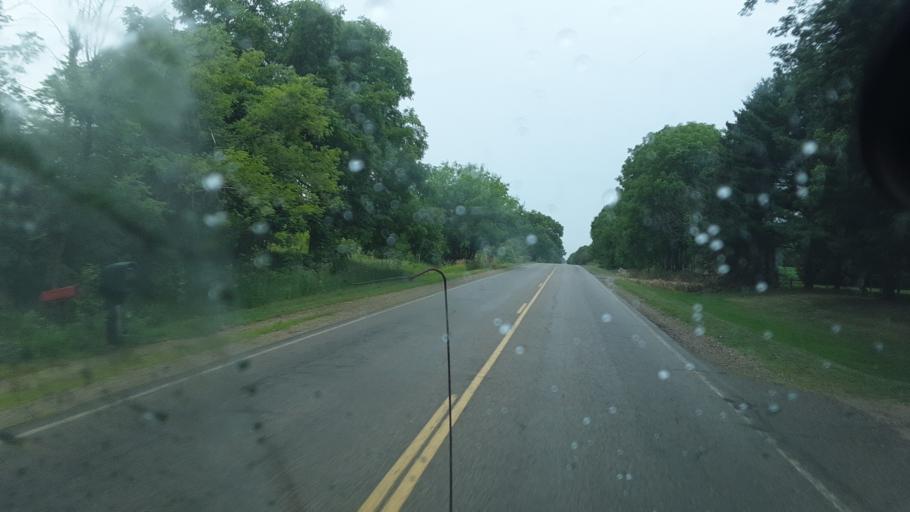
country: US
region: Michigan
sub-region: Hillsdale County
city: Reading
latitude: 41.7079
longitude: -84.7740
